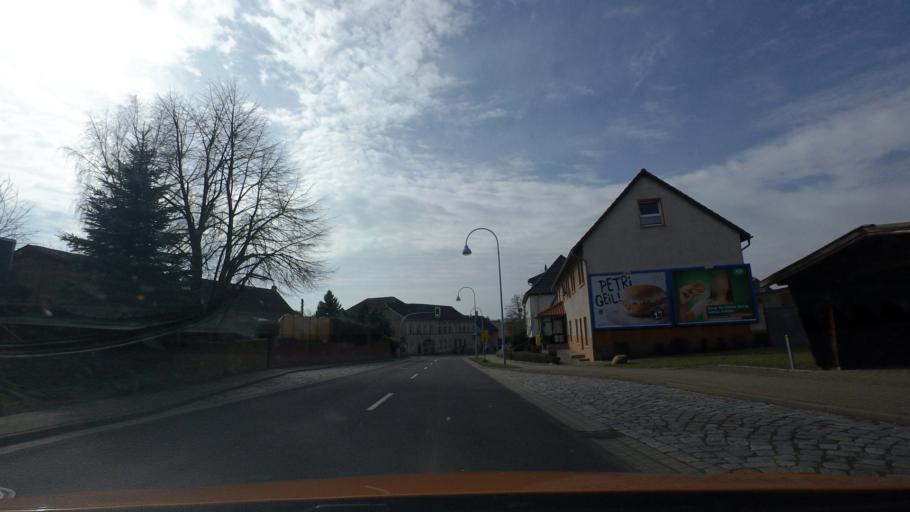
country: DE
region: Saxony-Anhalt
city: Wefensleben
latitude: 52.2139
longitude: 11.1425
